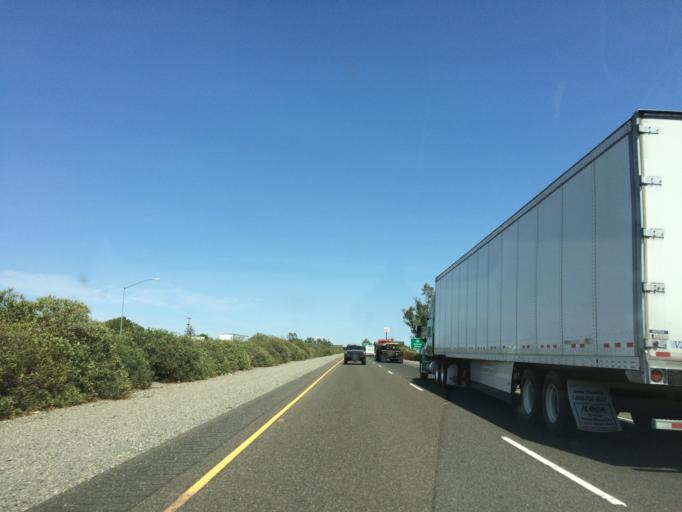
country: US
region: California
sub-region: Glenn County
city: Orland
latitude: 39.7421
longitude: -122.2056
